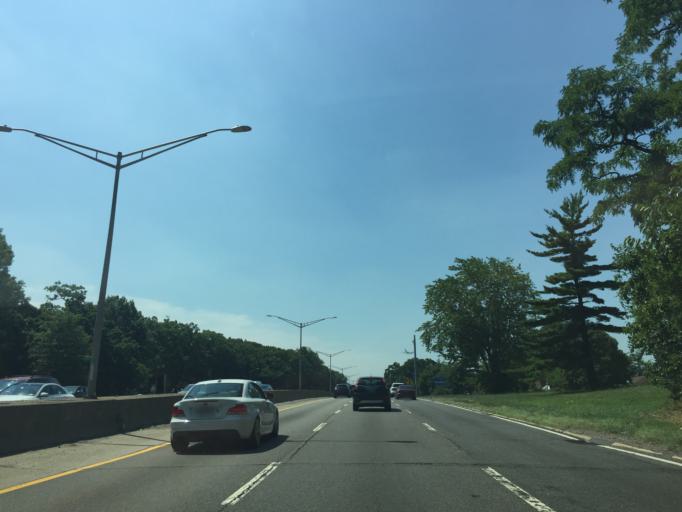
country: US
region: New York
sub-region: Nassau County
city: Bellerose Terrace
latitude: 40.7056
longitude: -73.7275
